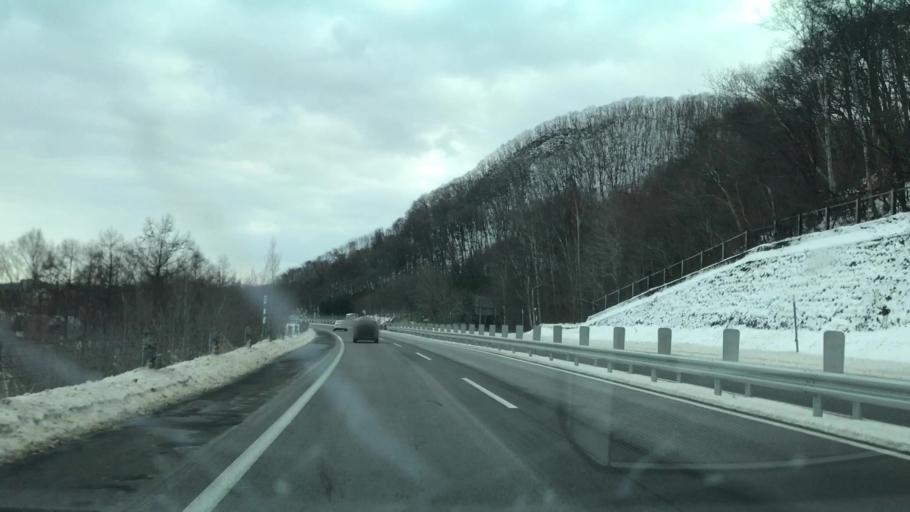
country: JP
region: Hokkaido
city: Sapporo
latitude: 43.1297
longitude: 141.1864
